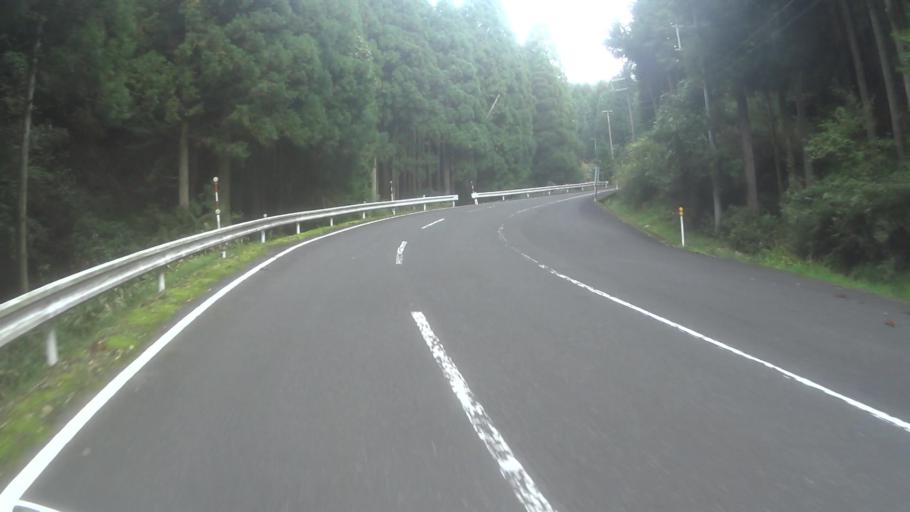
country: JP
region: Kyoto
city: Miyazu
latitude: 35.5305
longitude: 135.1255
